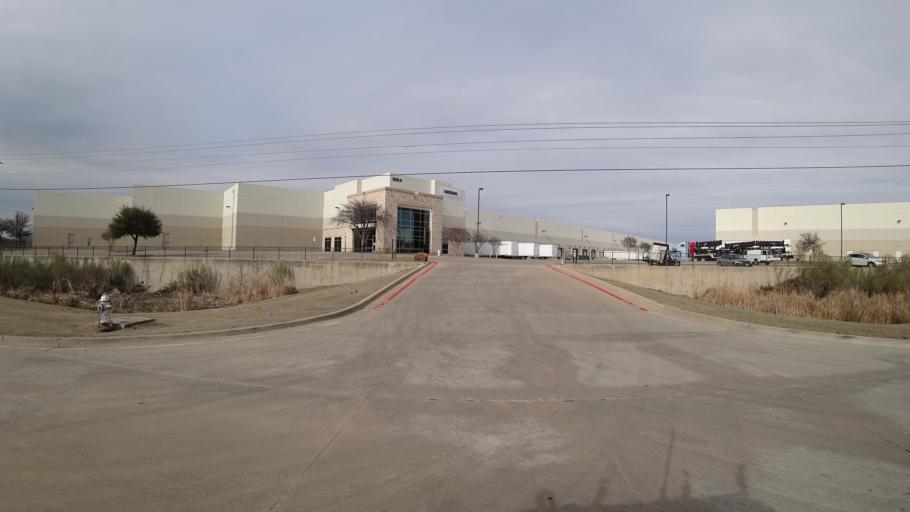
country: US
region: Texas
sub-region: Denton County
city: The Colony
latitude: 33.0548
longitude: -96.9168
